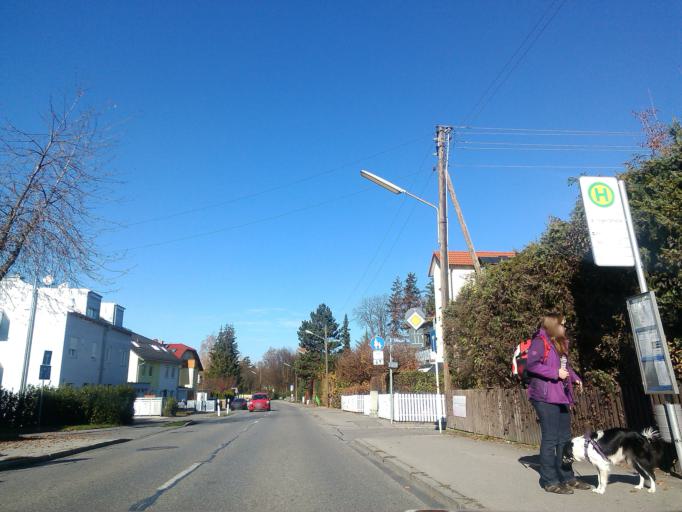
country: DE
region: Bavaria
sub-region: Upper Bavaria
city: Germering
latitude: 48.1676
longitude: 11.4110
